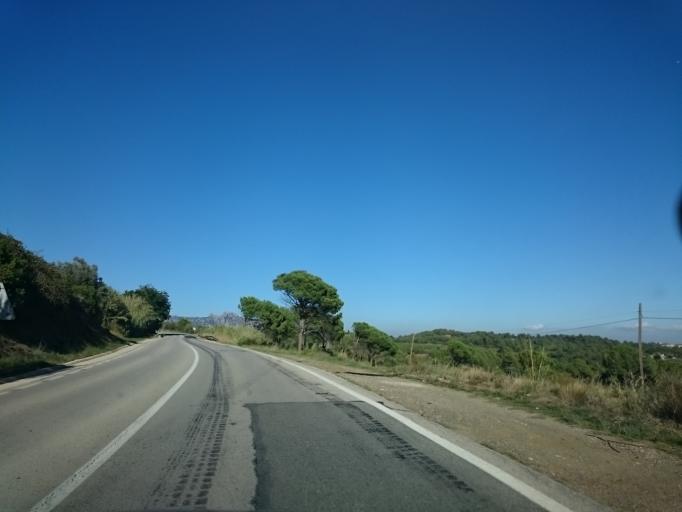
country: ES
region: Catalonia
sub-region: Provincia de Barcelona
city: Capellades
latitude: 41.5249
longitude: 1.7139
